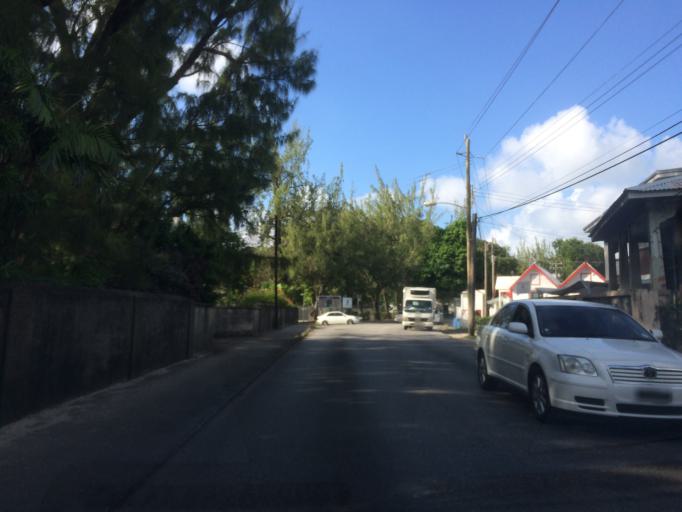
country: BB
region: Saint James
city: Holetown
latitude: 13.1911
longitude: -59.6383
